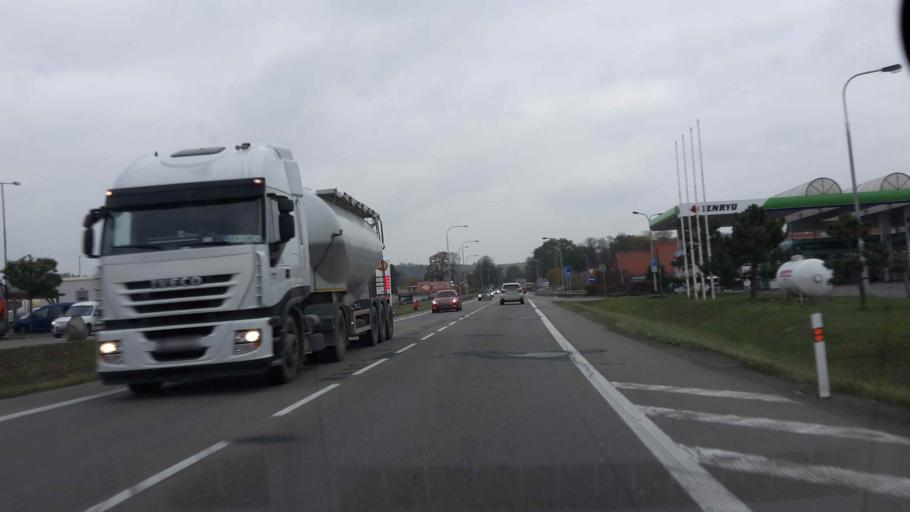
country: CZ
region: South Moravian
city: Slavkov u Brna
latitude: 49.1496
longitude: 16.8659
